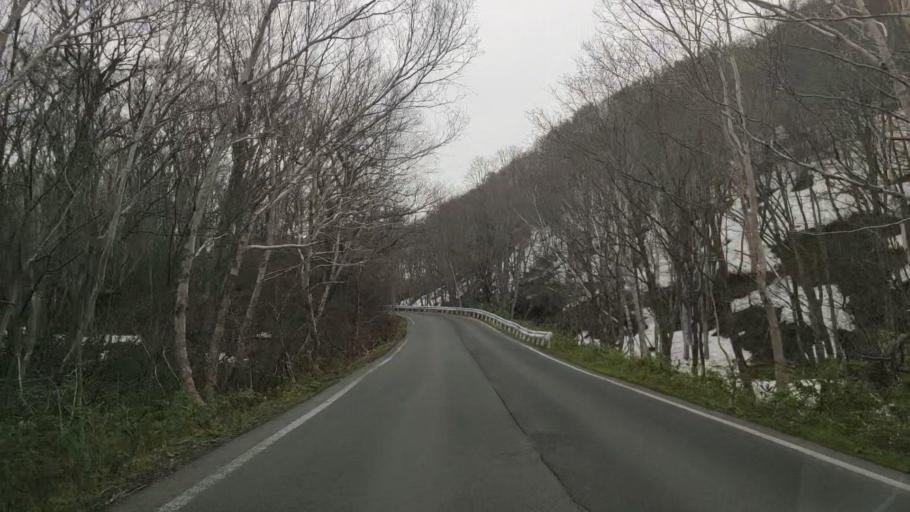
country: JP
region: Aomori
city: Aomori Shi
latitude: 40.6915
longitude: 140.9114
